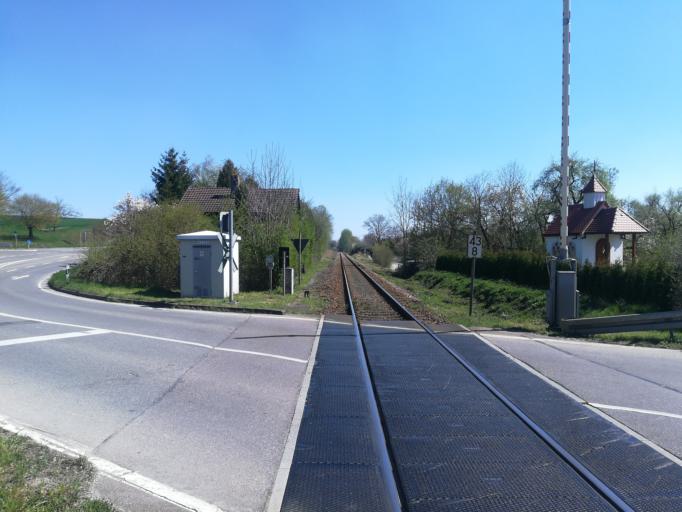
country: DE
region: Baden-Wuerttemberg
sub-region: Tuebingen Region
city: Munderkingen
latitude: 48.2335
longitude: 9.6581
